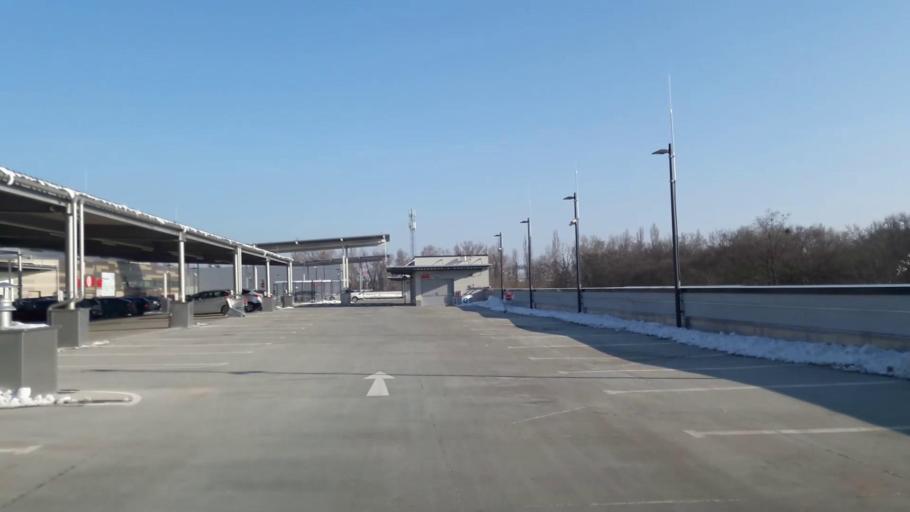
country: AT
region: Lower Austria
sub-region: Politischer Bezirk Wien-Umgebung
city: Schwechat
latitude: 48.1685
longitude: 16.4735
